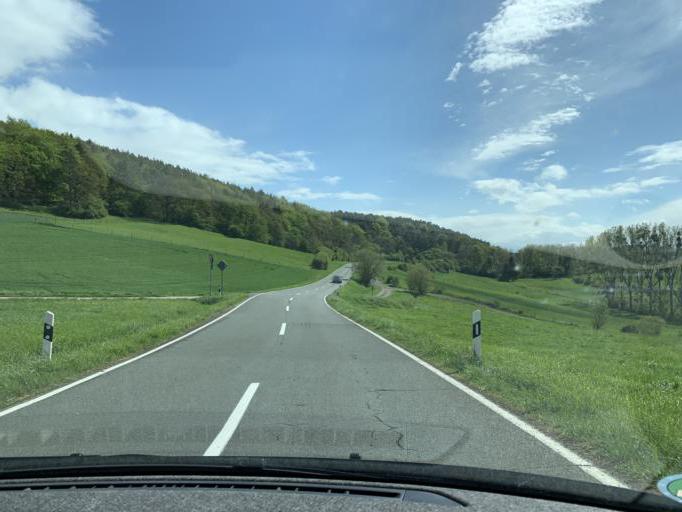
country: DE
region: North Rhine-Westphalia
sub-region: Regierungsbezirk Koln
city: Mechernich
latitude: 50.5752
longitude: 6.6987
